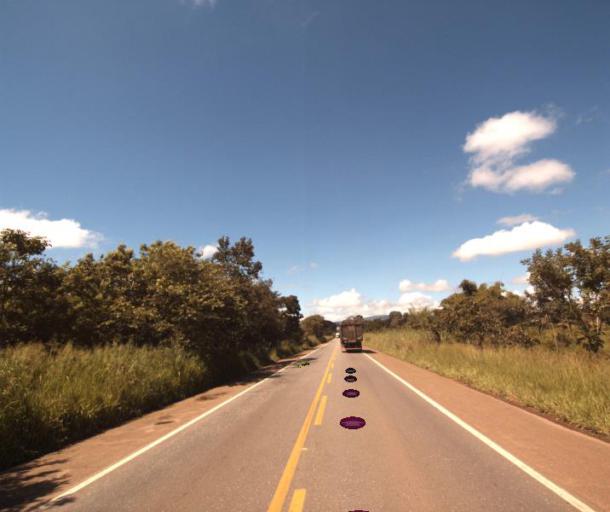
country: BR
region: Goias
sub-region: Jaragua
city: Jaragua
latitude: -15.7152
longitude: -49.3297
